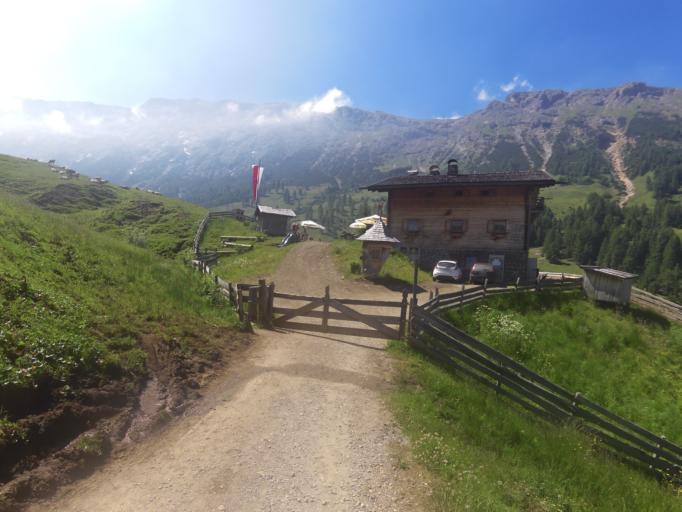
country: IT
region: Trentino-Alto Adige
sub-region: Bolzano
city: Siusi
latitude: 46.5142
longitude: 11.6073
